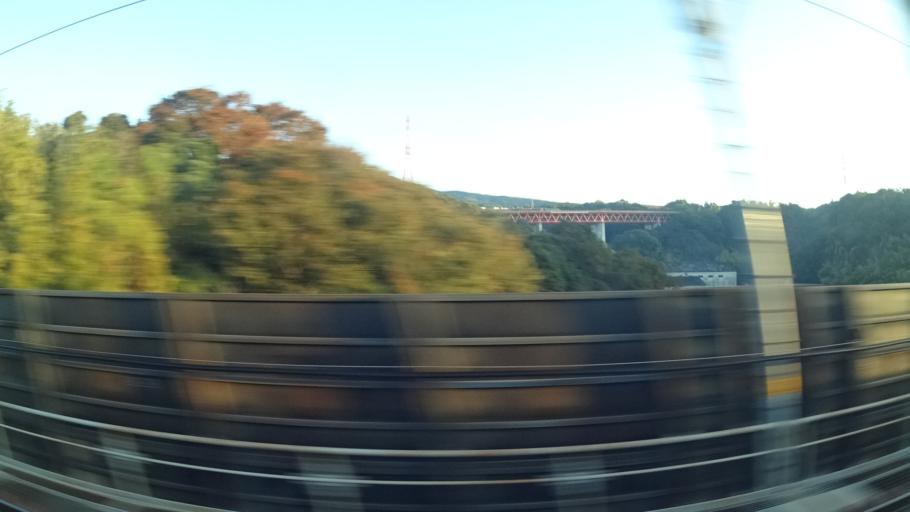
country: JP
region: Shizuoka
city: Numazu
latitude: 35.1439
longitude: 138.8028
